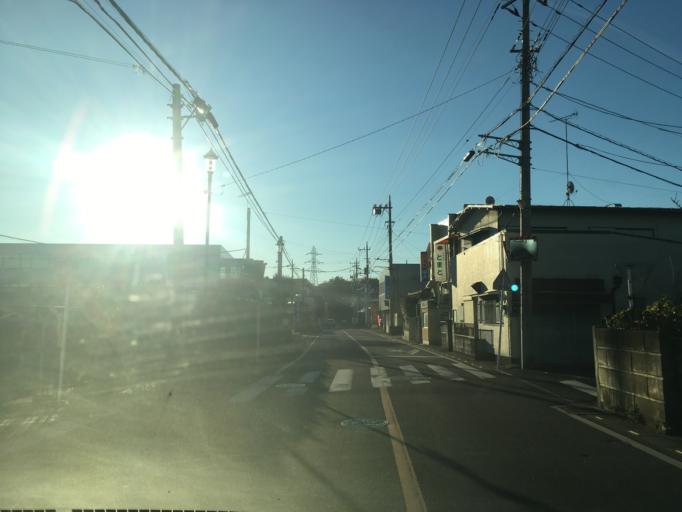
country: JP
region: Saitama
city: Tokorozawa
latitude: 35.8031
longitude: 139.4195
